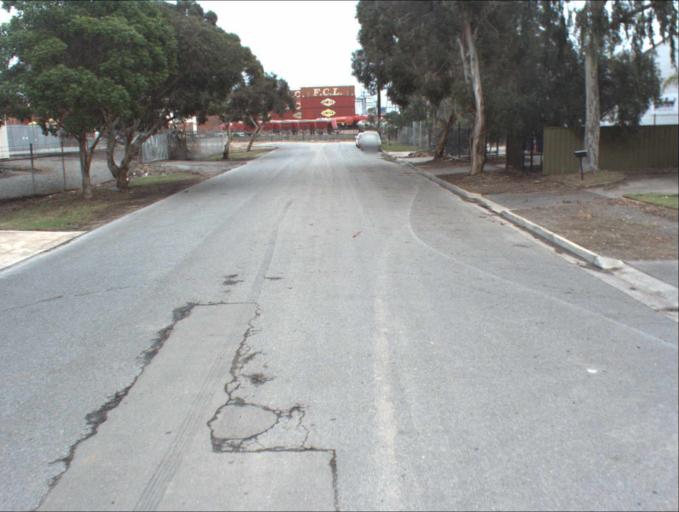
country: AU
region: South Australia
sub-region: Port Adelaide Enfield
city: Blair Athol
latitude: -34.8470
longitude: 138.5813
